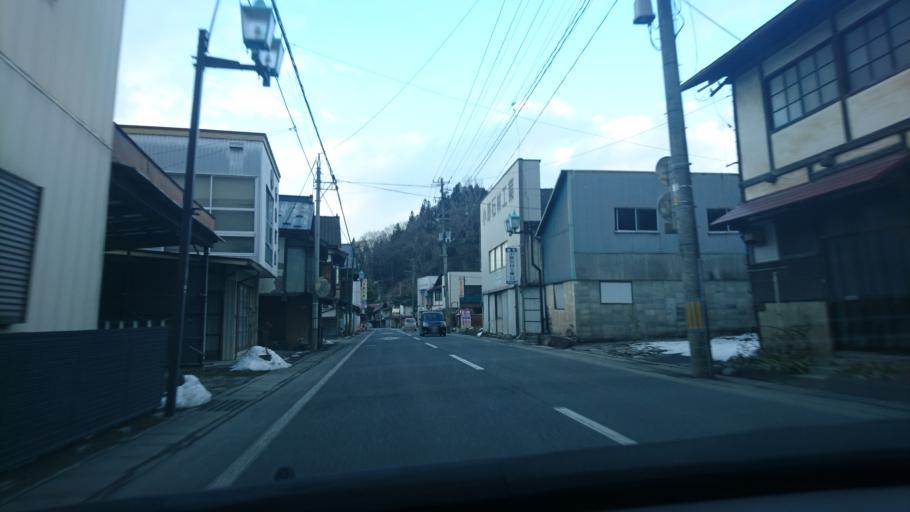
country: JP
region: Iwate
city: Ichinoseki
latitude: 38.9908
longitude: 141.3315
